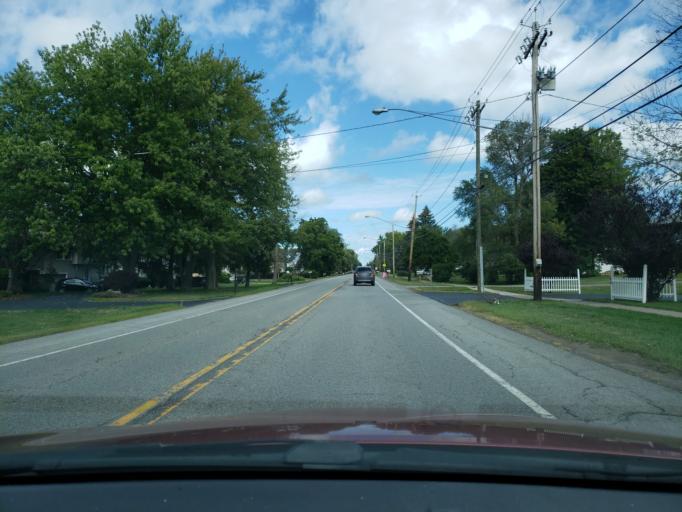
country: US
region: New York
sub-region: Monroe County
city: Greece
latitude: 43.2201
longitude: -77.7338
